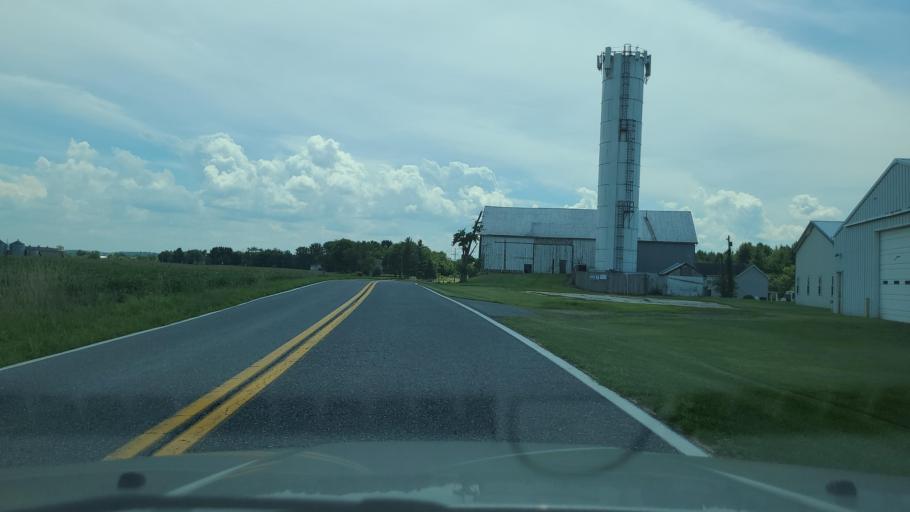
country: US
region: Maryland
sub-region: Frederick County
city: Thurmont
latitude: 39.5866
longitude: -77.3726
